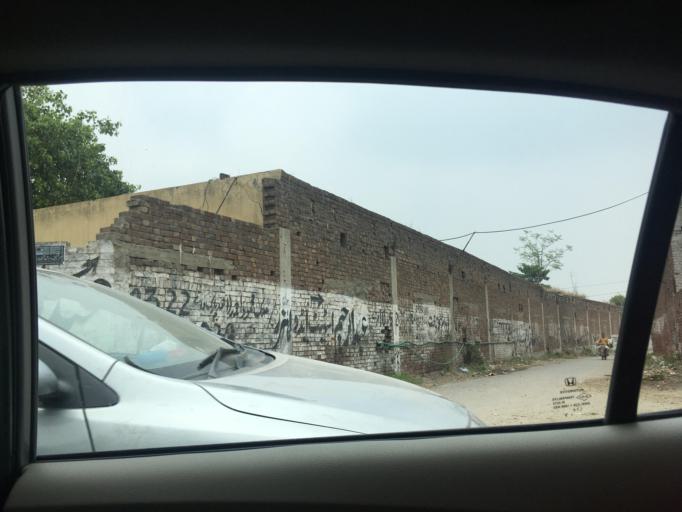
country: PK
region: Punjab
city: Lahore
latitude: 31.6090
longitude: 74.3526
